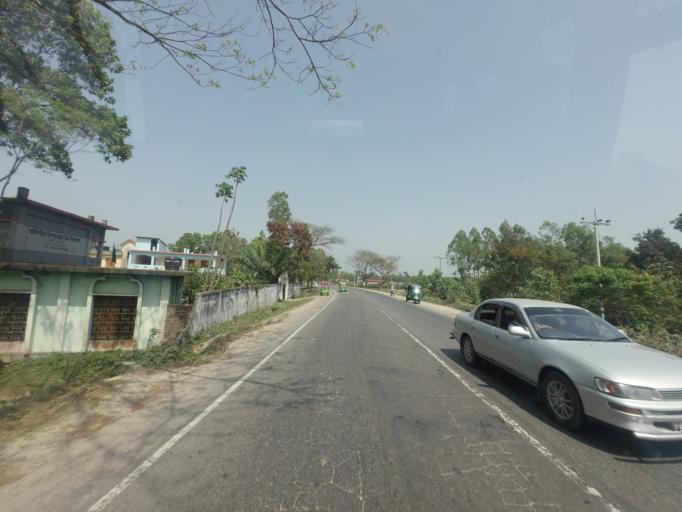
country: BD
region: Sylhet
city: Habiganj
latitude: 24.1277
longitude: 91.3199
